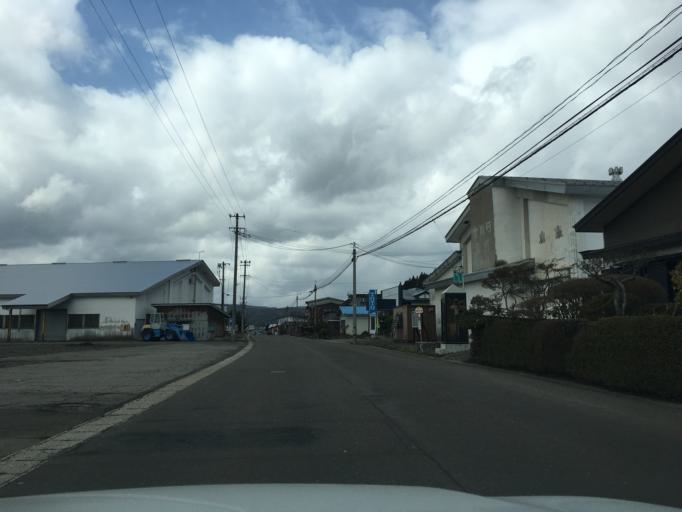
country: JP
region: Akita
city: Takanosu
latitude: 40.1625
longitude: 140.3269
